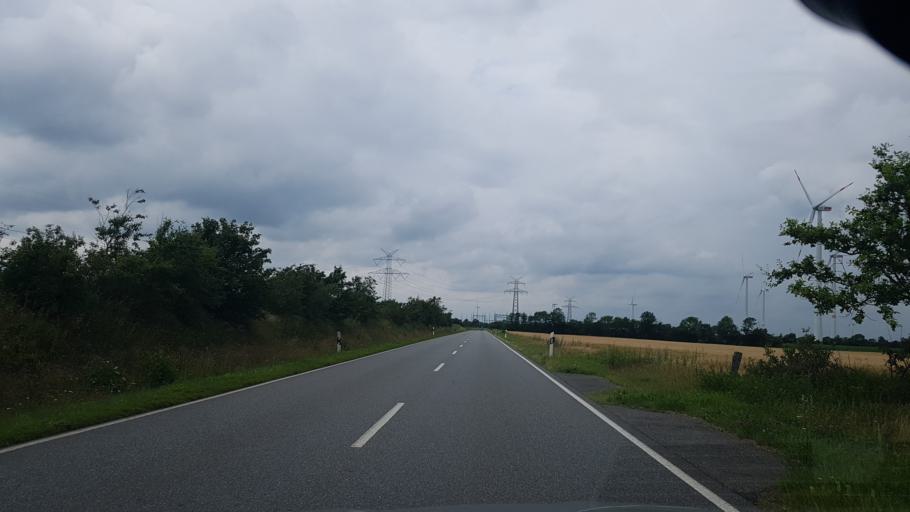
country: DE
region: Schleswig-Holstein
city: Jardelund
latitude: 54.8434
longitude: 9.2075
